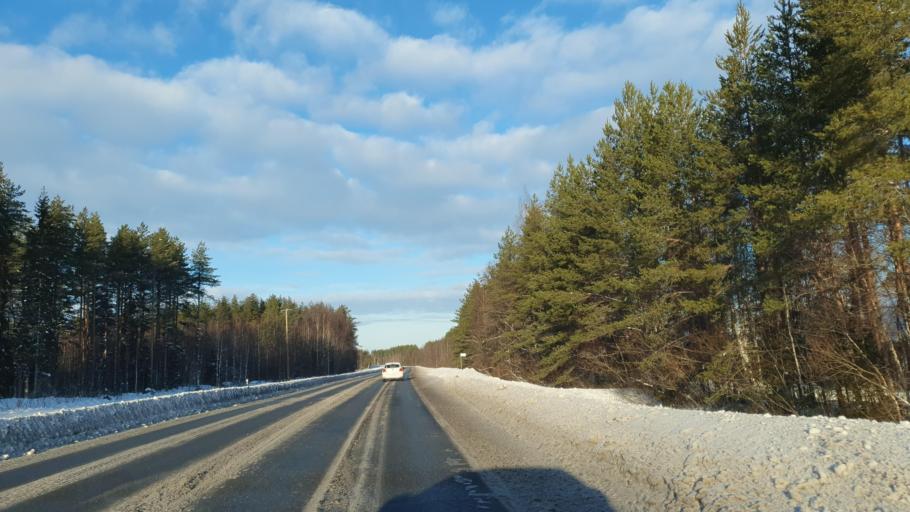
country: FI
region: Northern Ostrobothnia
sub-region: Oulunkaari
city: Utajaervi
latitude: 64.7815
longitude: 26.2660
